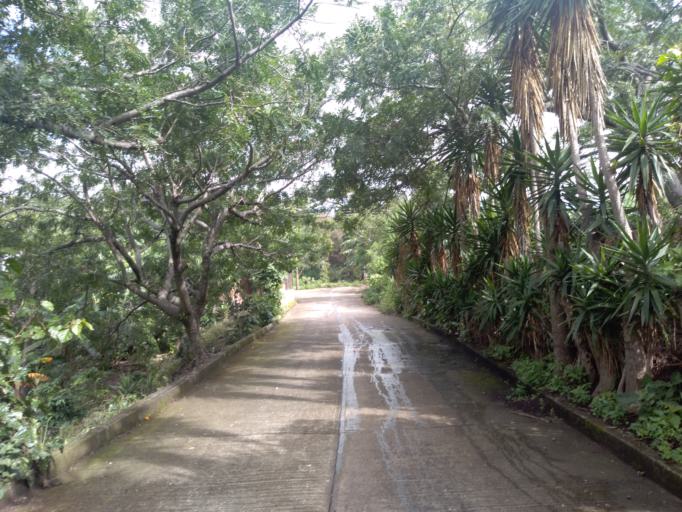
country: GT
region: Escuintla
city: San Vicente Pacaya
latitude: 14.3713
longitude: -90.5678
